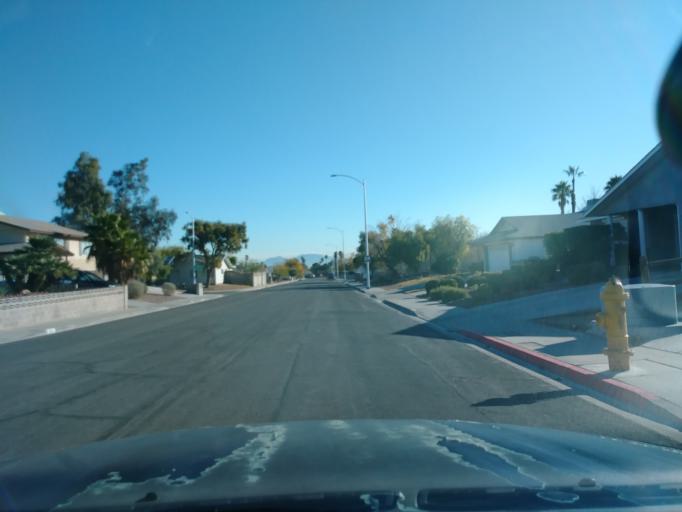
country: US
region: Nevada
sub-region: Clark County
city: Spring Valley
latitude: 36.1702
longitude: -115.2506
